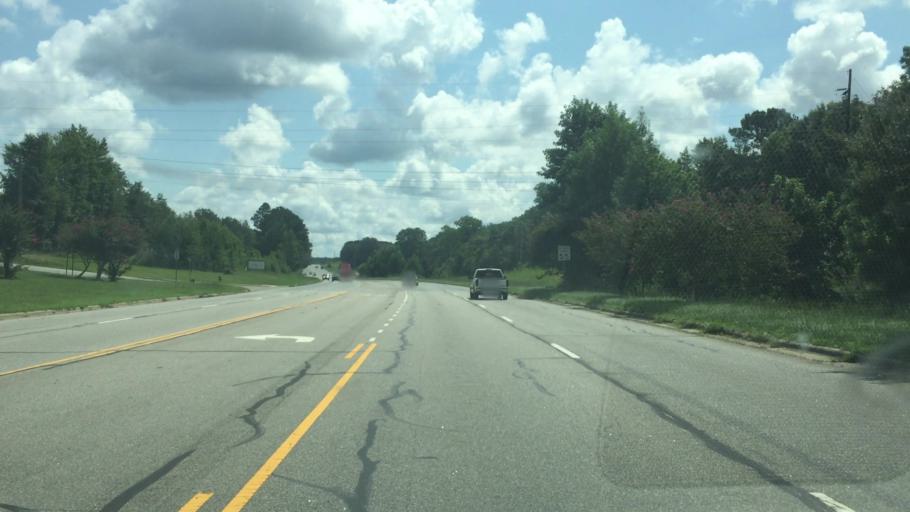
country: US
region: North Carolina
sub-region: Anson County
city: Wadesboro
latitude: 34.9632
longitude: -80.0397
